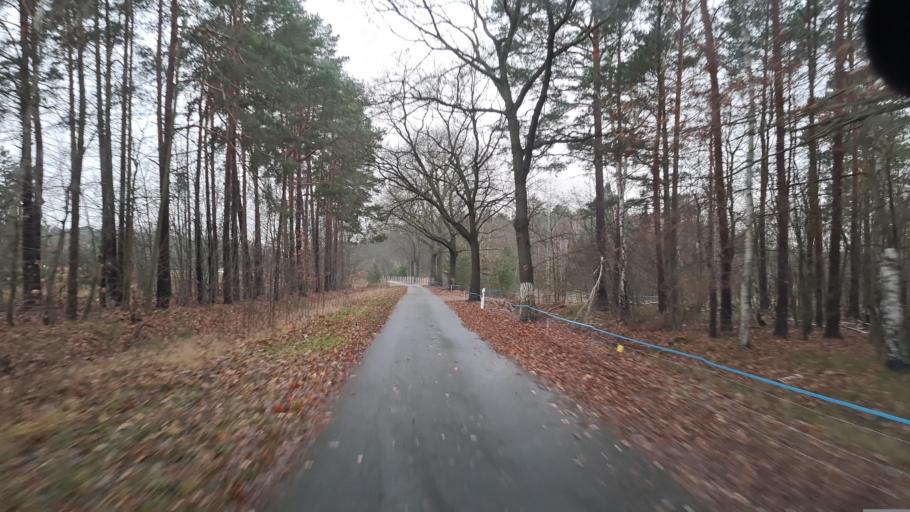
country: DE
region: Brandenburg
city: Neupetershain
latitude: 51.6330
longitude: 14.1810
